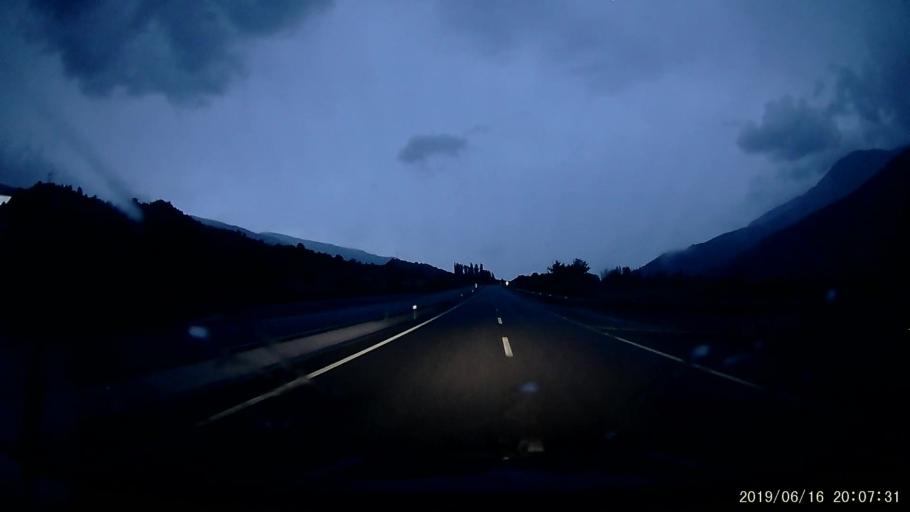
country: TR
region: Sivas
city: Dogansar
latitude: 40.3186
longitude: 37.6224
